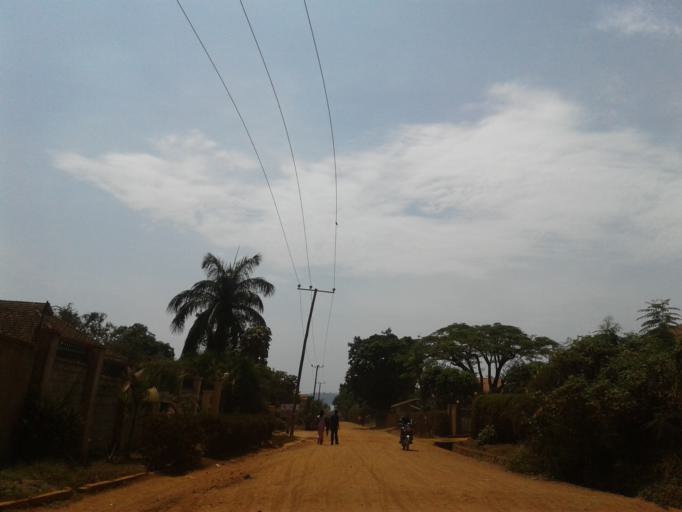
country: UG
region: Central Region
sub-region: Kampala District
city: Kampala
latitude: 0.2618
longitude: 32.6325
